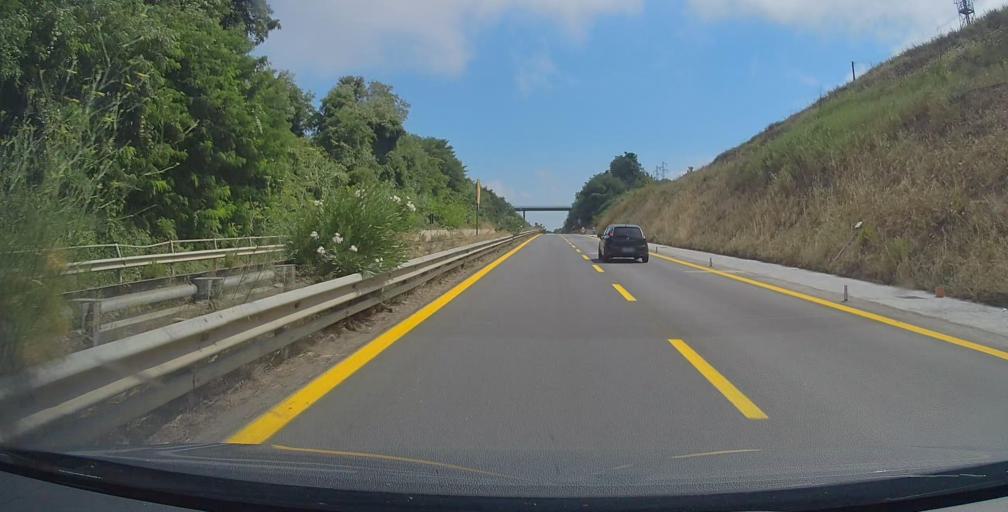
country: IT
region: Calabria
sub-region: Provincia di Vibo-Valentia
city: Sant'Onofrio
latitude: 38.7113
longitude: 16.1537
